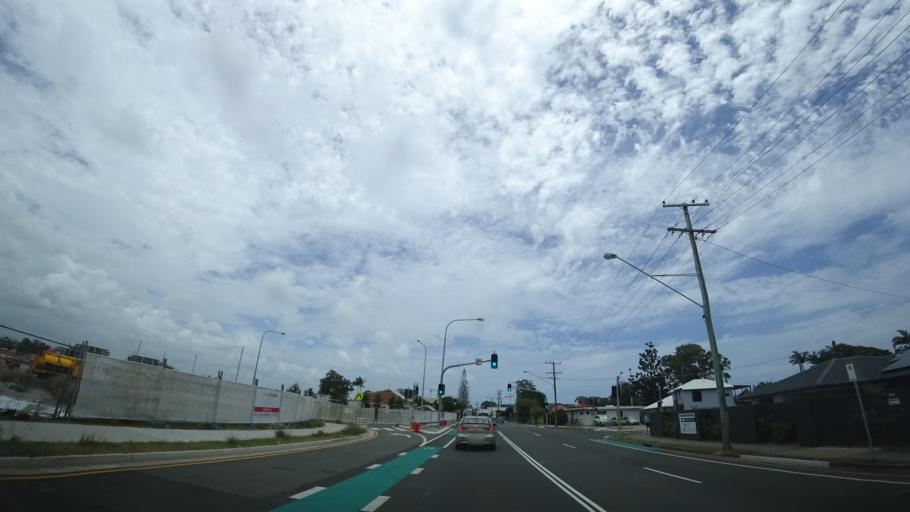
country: AU
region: Queensland
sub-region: Sunshine Coast
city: Mooloolaba
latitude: -26.6615
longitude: 153.0928
